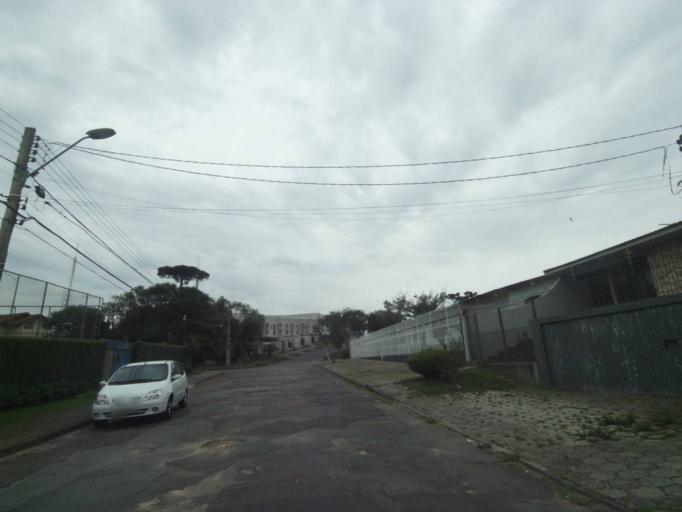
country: BR
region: Parana
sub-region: Curitiba
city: Curitiba
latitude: -25.3973
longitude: -49.2899
